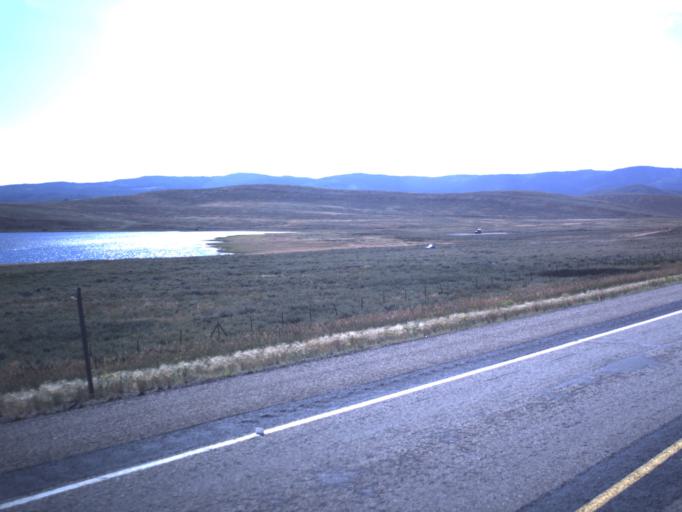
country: US
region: Utah
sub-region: Wasatch County
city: Heber
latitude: 40.2371
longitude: -111.1368
